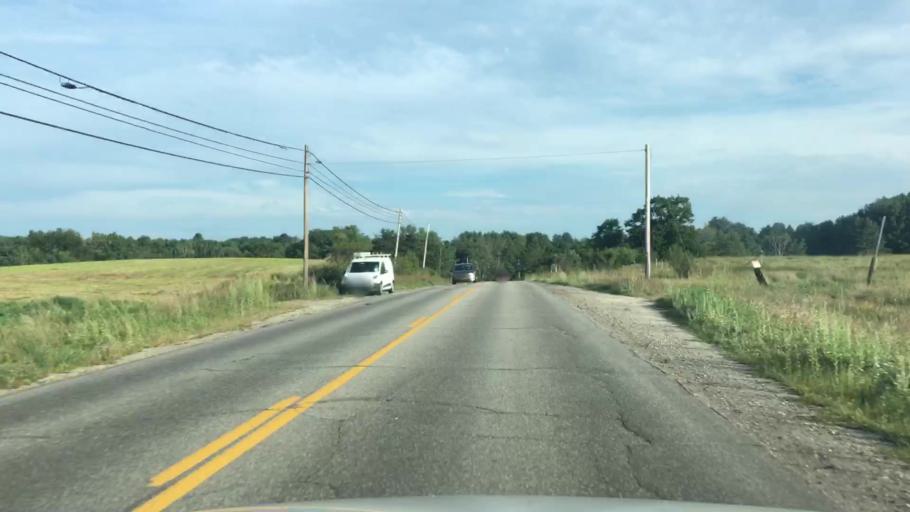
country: US
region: Maine
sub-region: Cumberland County
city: South Windham
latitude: 43.7283
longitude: -70.4083
